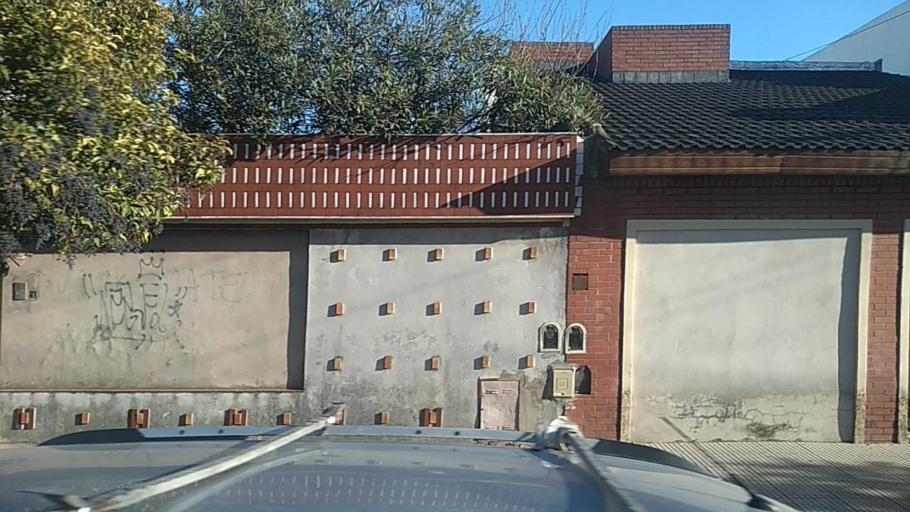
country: AR
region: Buenos Aires F.D.
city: Villa Santa Rita
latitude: -34.6263
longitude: -58.5024
